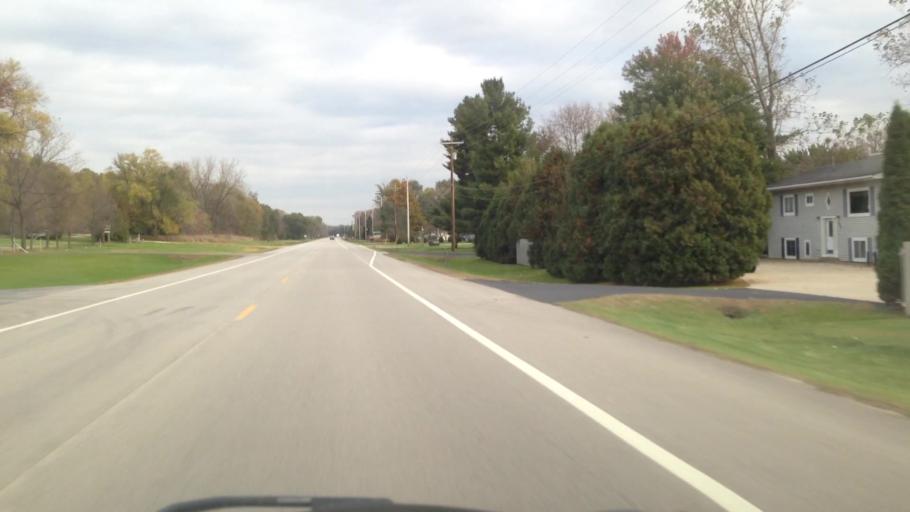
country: US
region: Minnesota
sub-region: Olmsted County
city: Rochester
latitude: 43.9718
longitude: -92.3895
